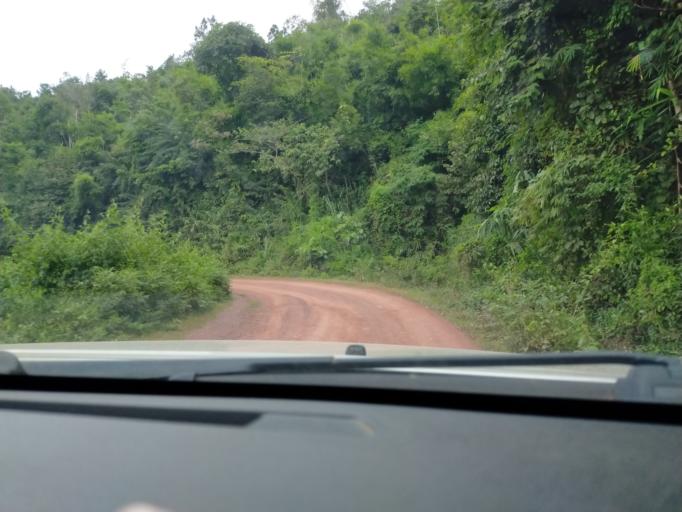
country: TH
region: Nan
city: Chaloem Phra Kiat
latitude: 19.7693
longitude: 101.3496
